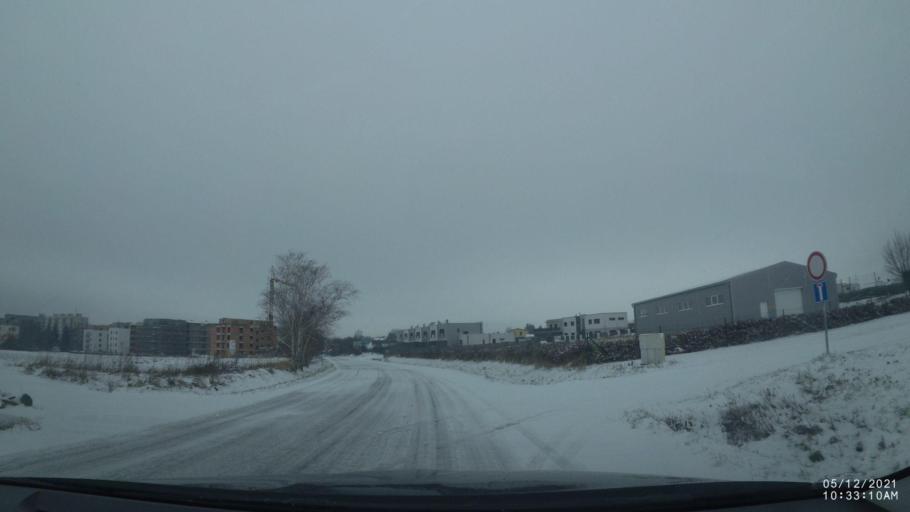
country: CZ
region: Kralovehradecky
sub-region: Okres Rychnov nad Kneznou
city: Rychnov nad Kneznou
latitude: 50.1639
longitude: 16.2917
